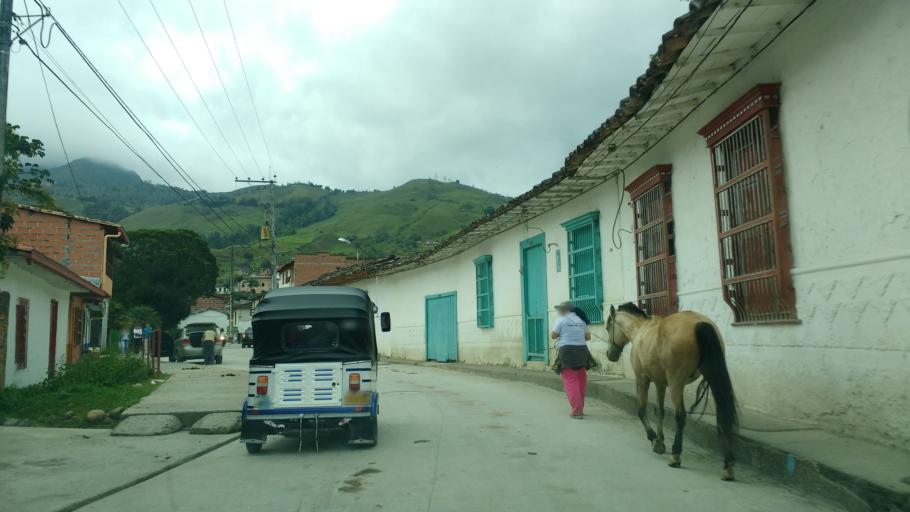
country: CO
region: Antioquia
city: Concepcion
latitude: 6.3942
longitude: -75.2560
